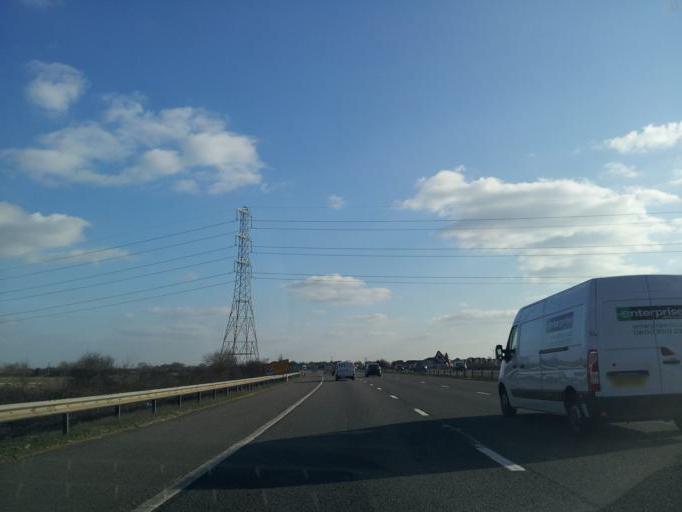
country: GB
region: England
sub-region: Somerset
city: Puriton
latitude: 51.1540
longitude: -2.9811
